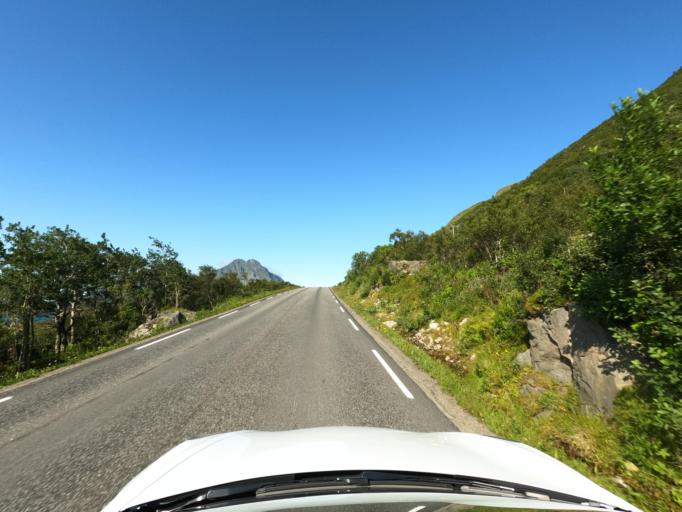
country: NO
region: Nordland
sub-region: Vagan
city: Kabelvag
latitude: 68.2210
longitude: 14.2160
